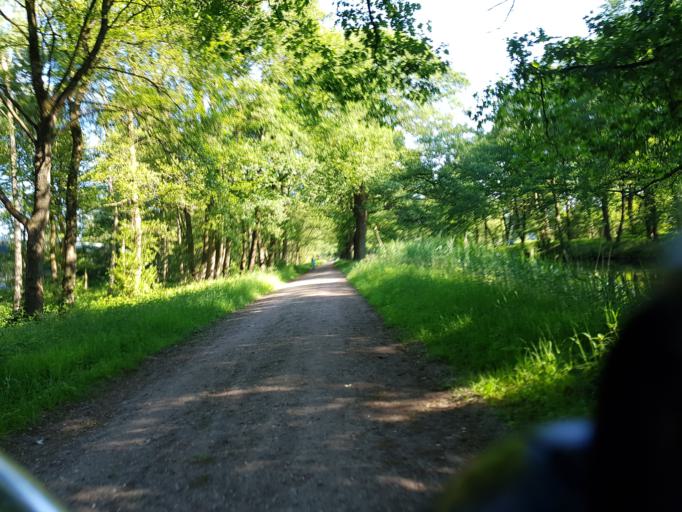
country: NL
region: Gelderland
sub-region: Gemeente Apeldoorn
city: Apeldoorn
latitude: 52.1838
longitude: 5.9891
